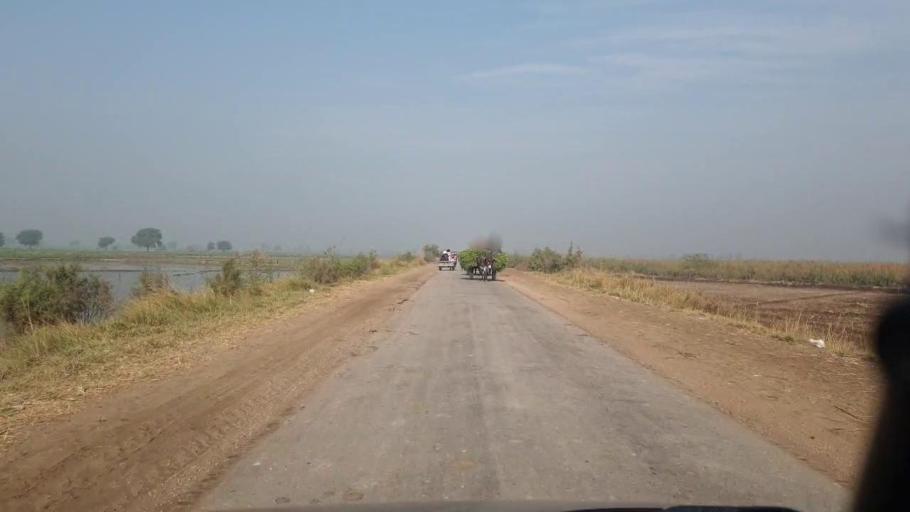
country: PK
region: Sindh
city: Shahdadpur
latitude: 25.9504
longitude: 68.5937
